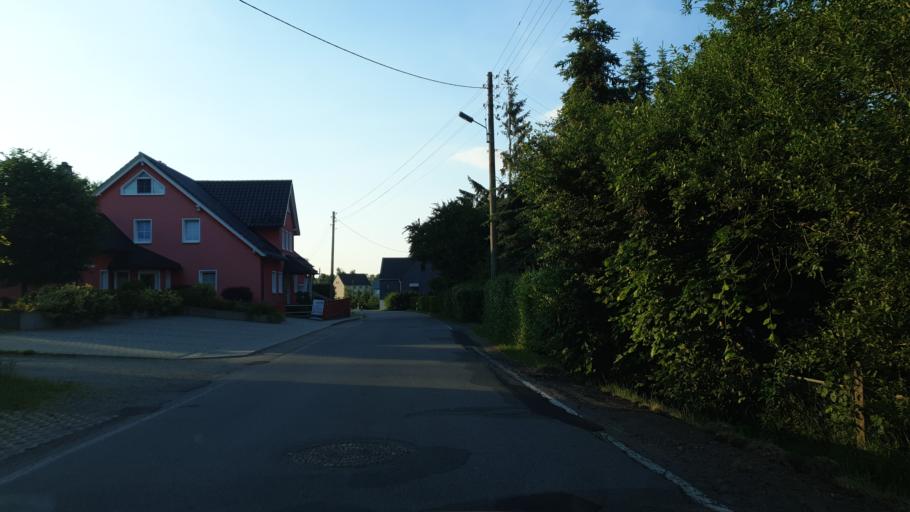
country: DE
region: Saxony
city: Stollberg
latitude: 50.6799
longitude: 12.7403
